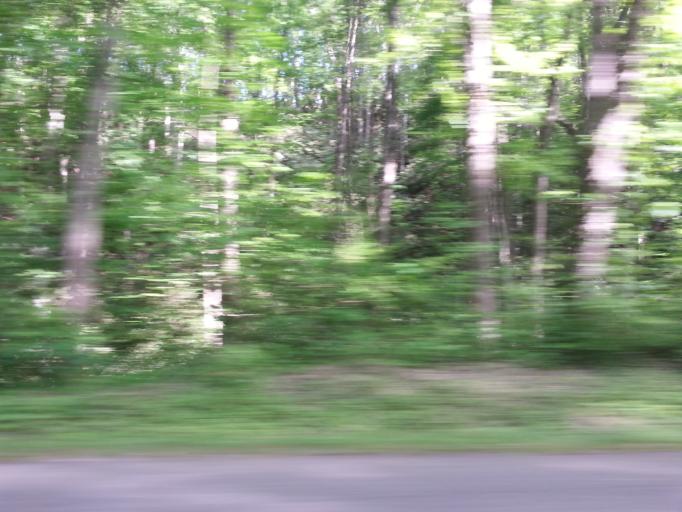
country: US
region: Tennessee
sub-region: Sevier County
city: Gatlinburg
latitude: 35.6679
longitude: -83.5924
